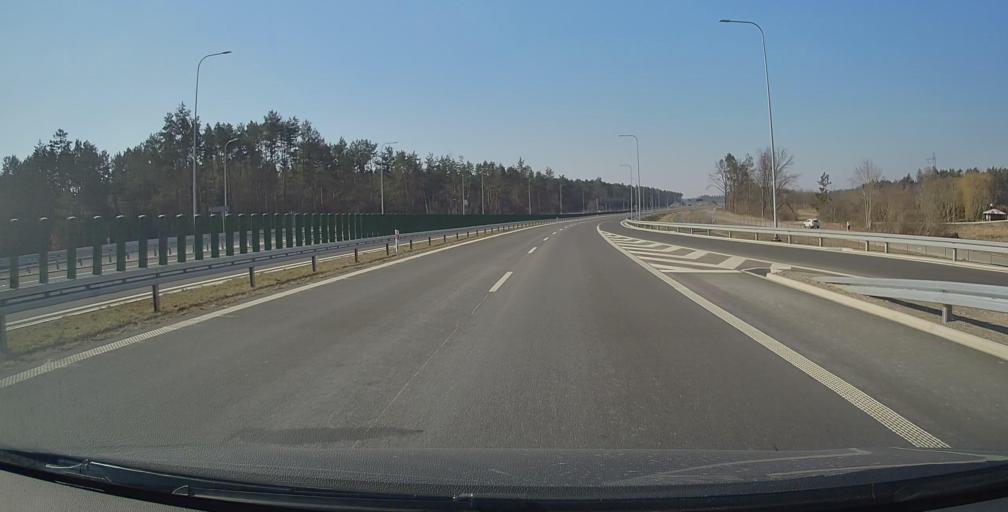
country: PL
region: Lublin Voivodeship
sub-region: Powiat janowski
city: Janow Lubelski
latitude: 50.6922
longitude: 22.3727
